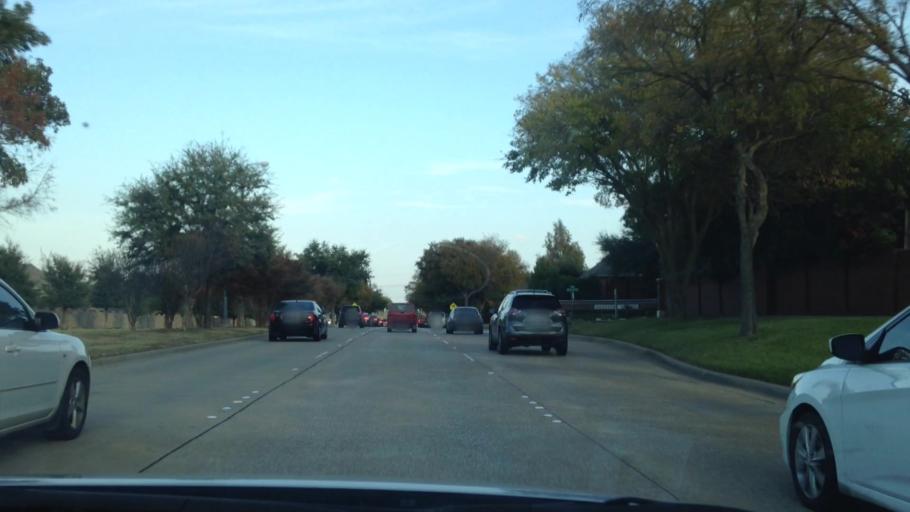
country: US
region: Texas
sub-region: Collin County
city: Plano
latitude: 33.0562
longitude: -96.7839
